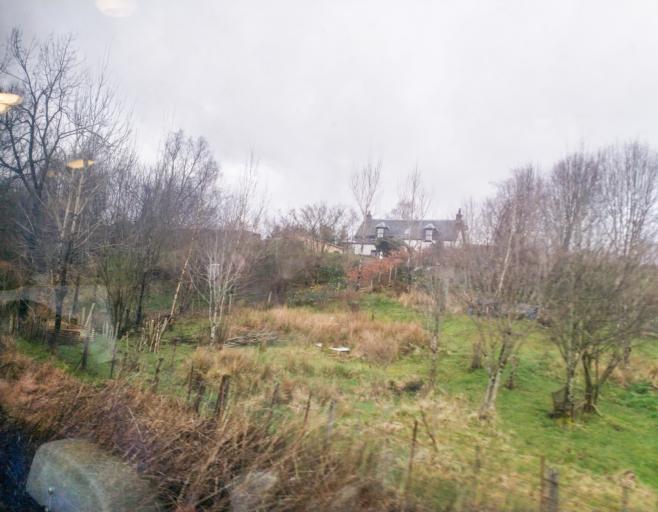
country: GB
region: Scotland
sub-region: Highland
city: Spean Bridge
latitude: 56.8889
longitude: -4.8651
